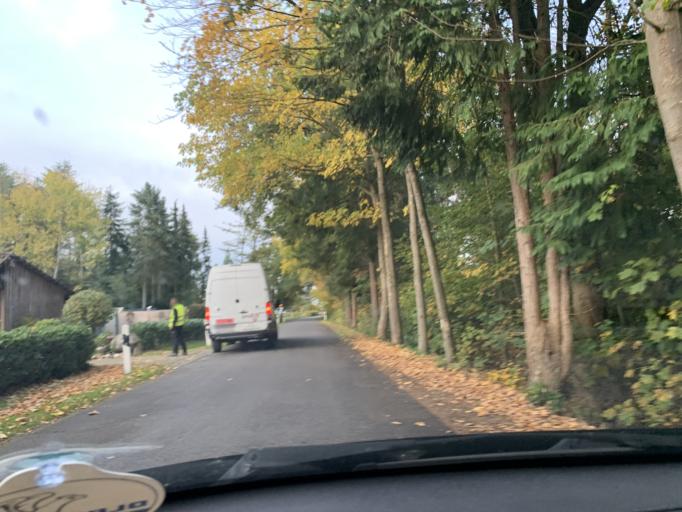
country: DE
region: Lower Saxony
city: Bad Zwischenahn
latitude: 53.2244
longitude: 8.0437
